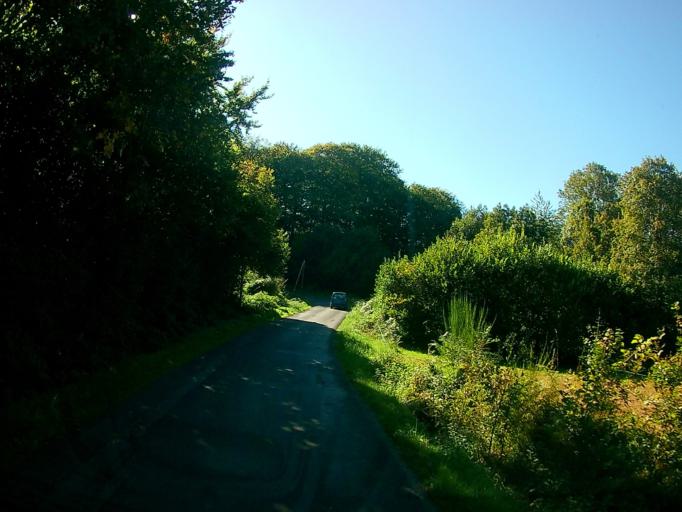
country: FR
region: Auvergne
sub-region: Departement du Puy-de-Dome
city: Chapdes-Beaufort
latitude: 45.8964
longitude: 2.8695
